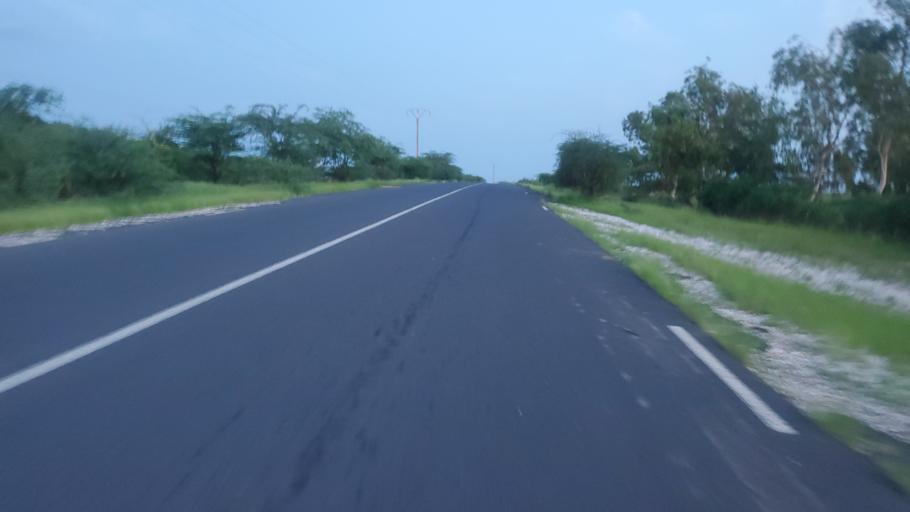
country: SN
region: Saint-Louis
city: Saint-Louis
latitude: 16.0768
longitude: -16.3900
